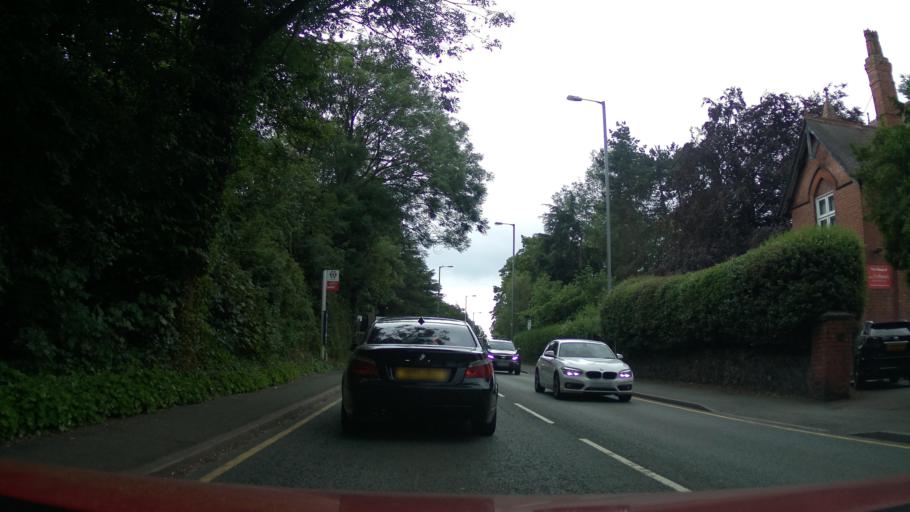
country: GB
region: England
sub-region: Wolverhampton
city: Wolverhampton
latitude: 52.5735
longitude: -2.1382
